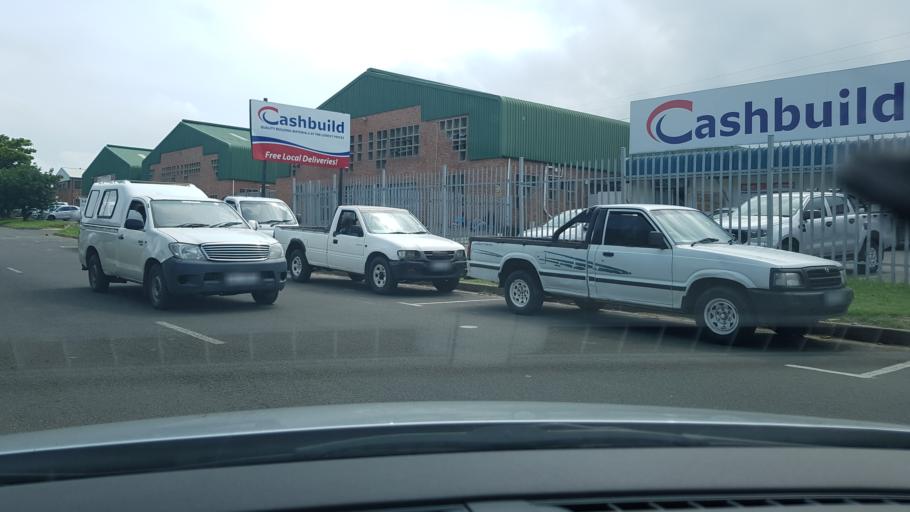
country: ZA
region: KwaZulu-Natal
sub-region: uThungulu District Municipality
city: Richards Bay
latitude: -28.7451
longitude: 32.0485
